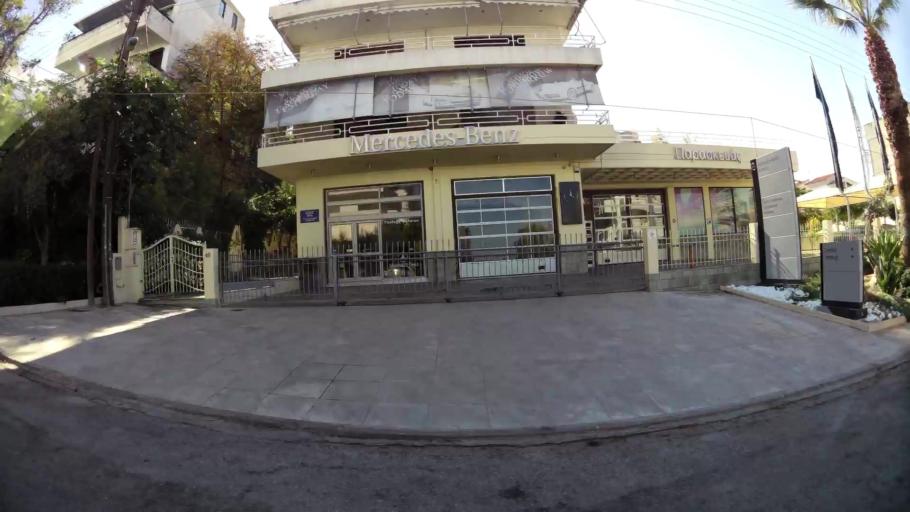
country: GR
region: Attica
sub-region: Nomarchia Athinas
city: Glyfada
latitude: 37.8648
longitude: 23.7675
